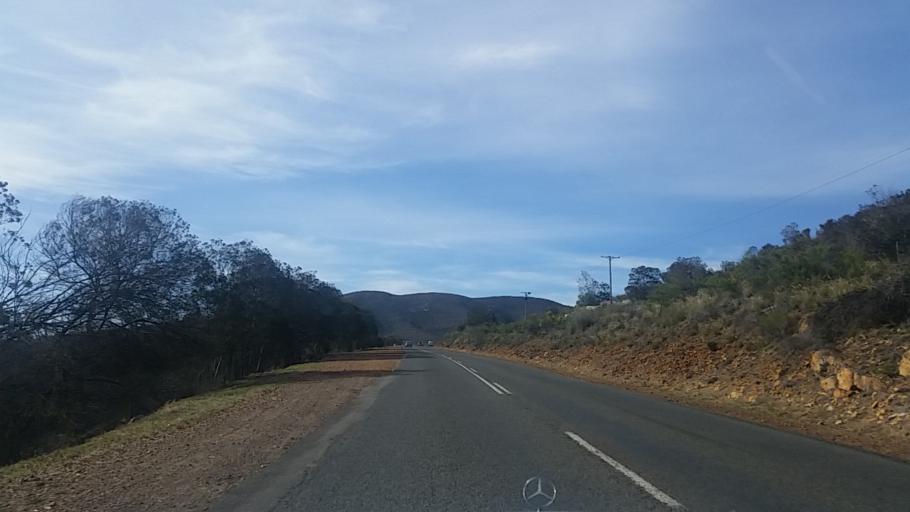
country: ZA
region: Western Cape
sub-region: Eden District Municipality
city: George
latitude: -33.8247
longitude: 22.3499
